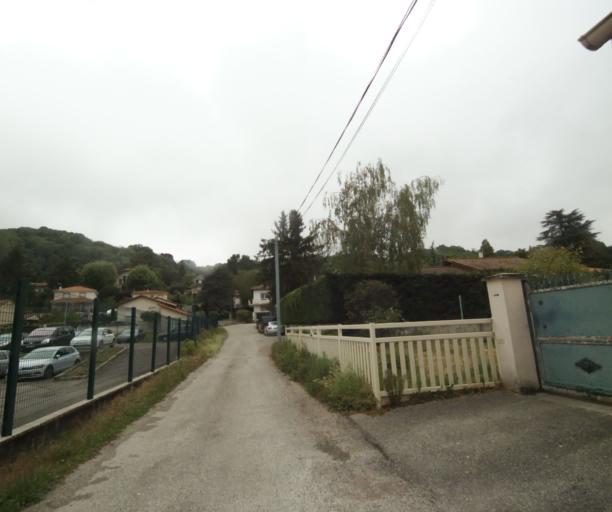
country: FR
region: Rhone-Alpes
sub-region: Departement de l'Ain
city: Miribel
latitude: 45.8216
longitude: 4.9432
